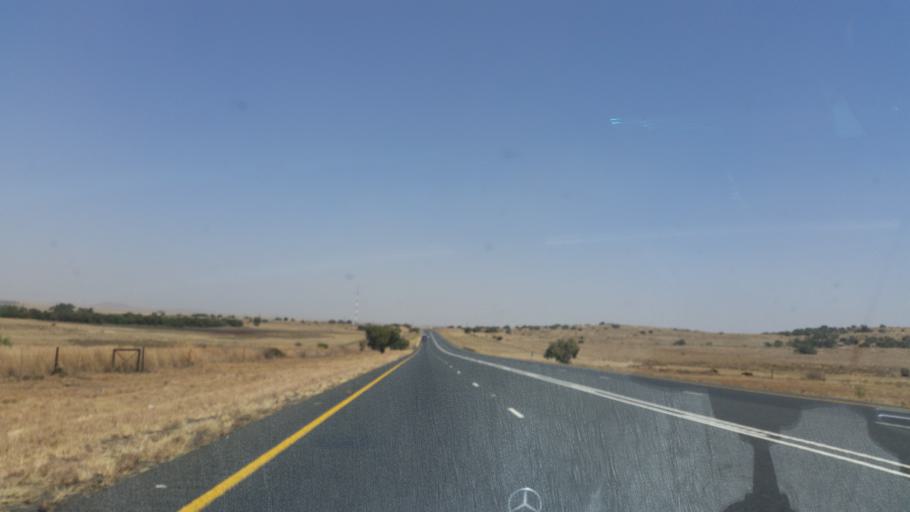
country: ZA
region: Orange Free State
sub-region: Lejweleputswa District Municipality
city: Winburg
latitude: -28.7093
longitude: 26.7857
